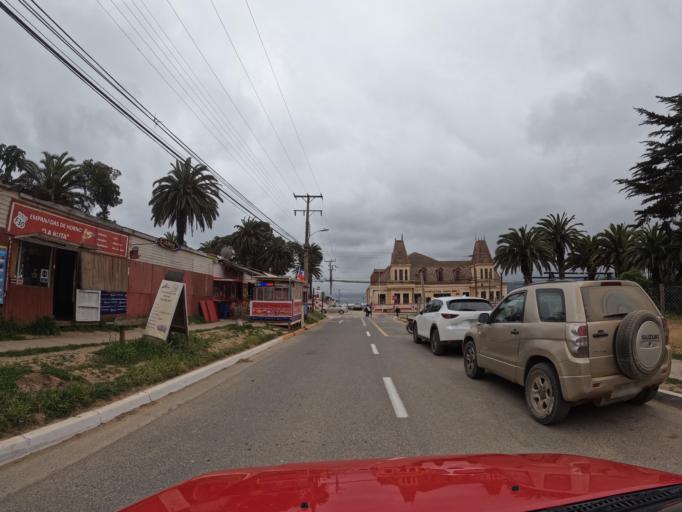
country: CL
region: O'Higgins
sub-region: Provincia de Colchagua
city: Santa Cruz
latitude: -34.3871
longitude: -72.0102
